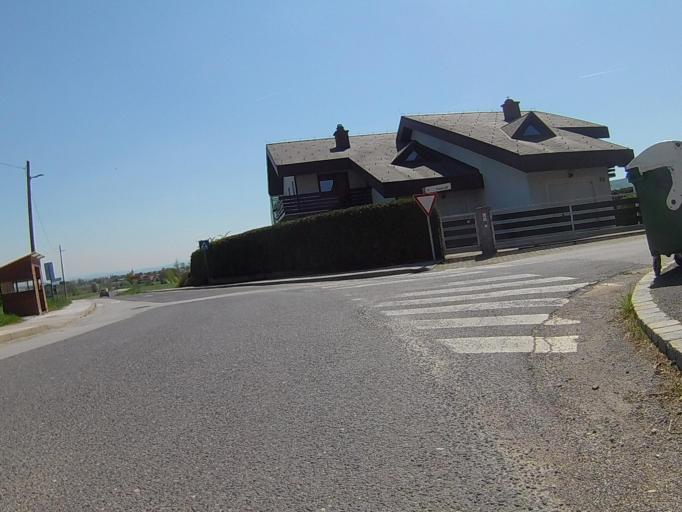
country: SI
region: Maribor
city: Razvanje
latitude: 46.5117
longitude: 15.6359
